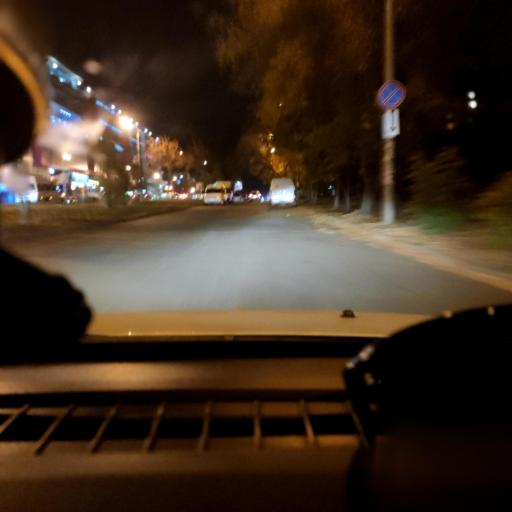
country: RU
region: Samara
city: Samara
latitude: 53.1892
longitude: 50.1916
